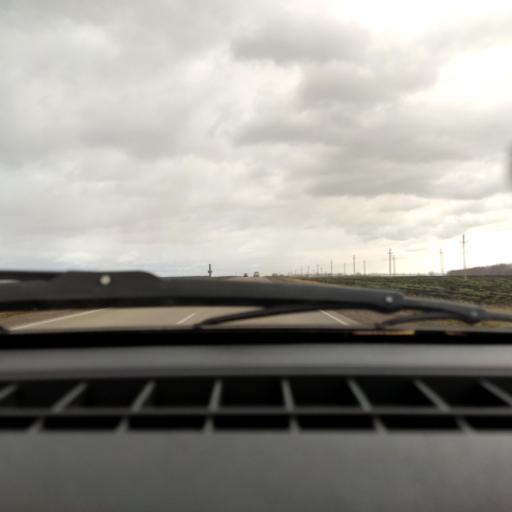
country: RU
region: Bashkortostan
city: Iglino
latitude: 54.7571
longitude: 56.2785
